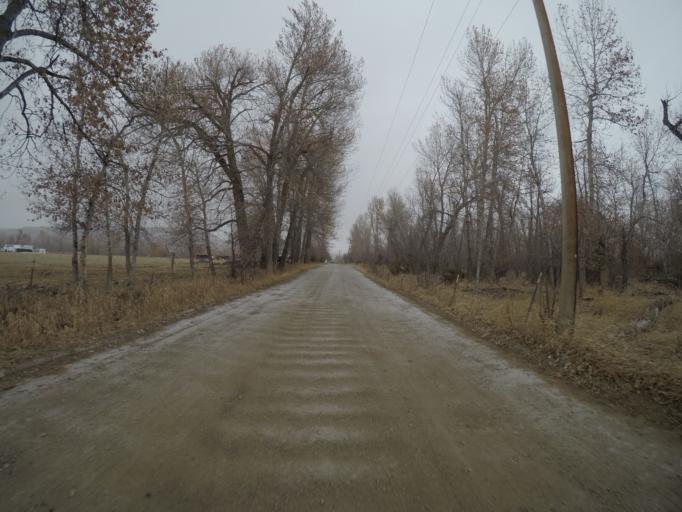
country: US
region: Montana
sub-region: Stillwater County
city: Absarokee
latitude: 45.5280
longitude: -109.4386
